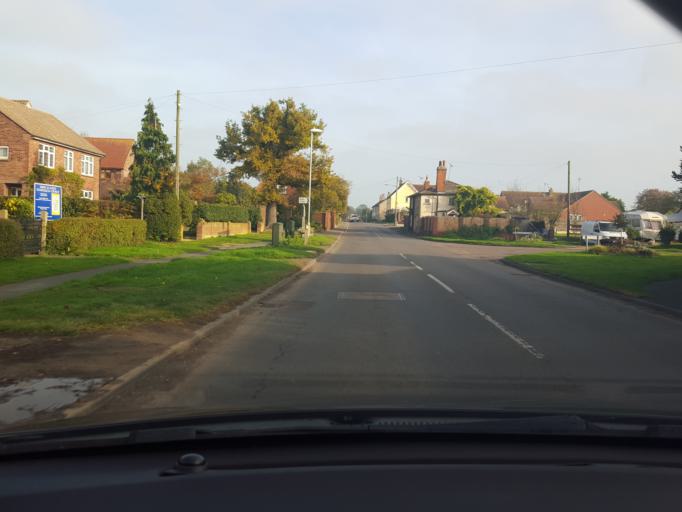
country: GB
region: England
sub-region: Essex
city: Frinton-on-Sea
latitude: 51.8525
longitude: 1.2250
